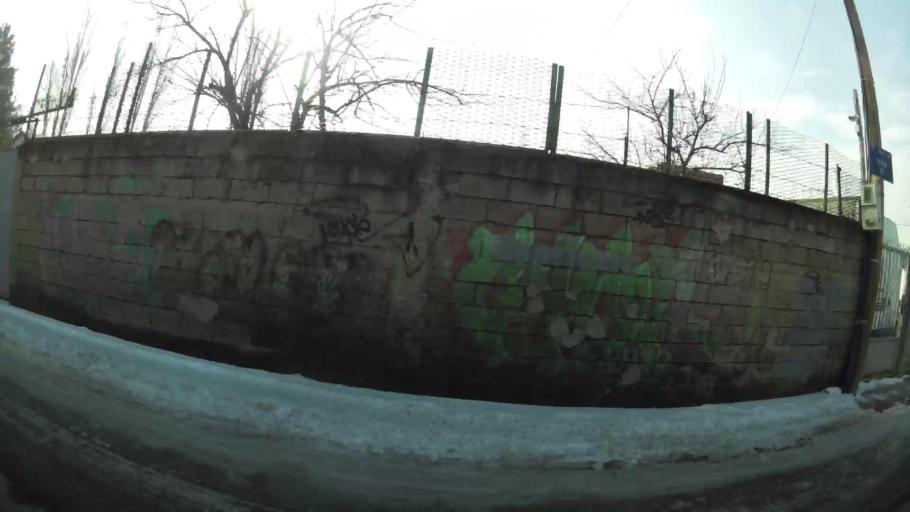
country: MK
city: Krushopek
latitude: 42.0158
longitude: 21.3778
